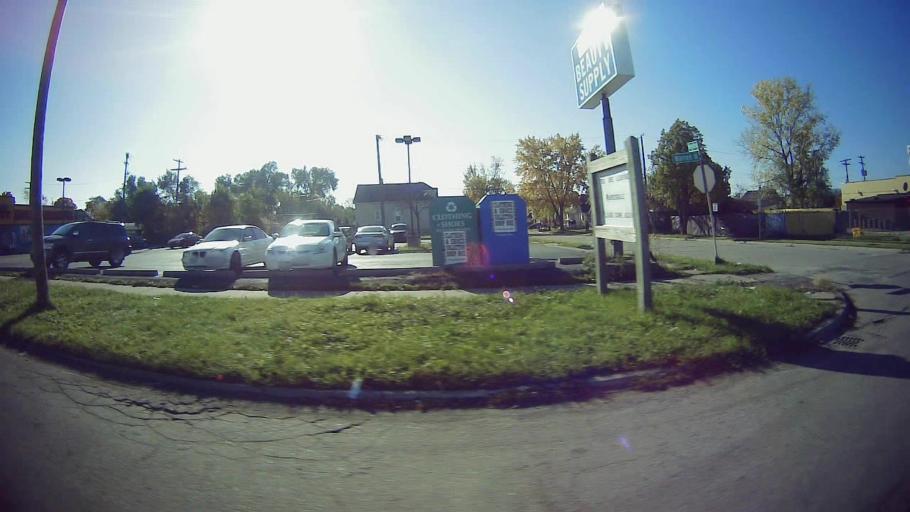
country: US
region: Michigan
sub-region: Wayne County
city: Dearborn Heights
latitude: 42.3431
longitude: -83.2378
